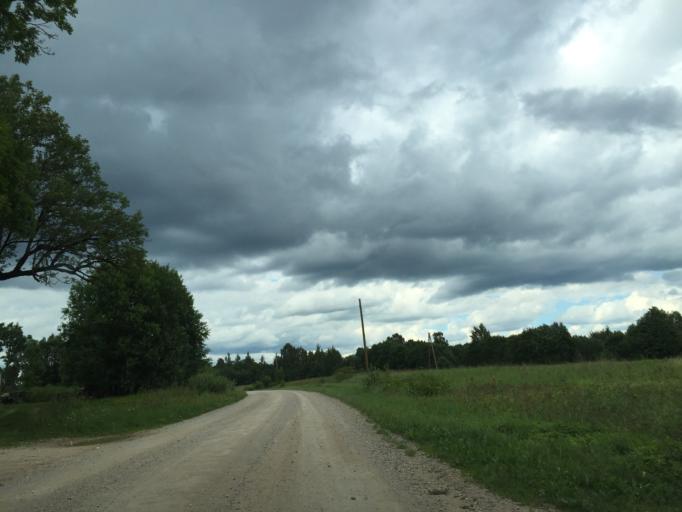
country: LV
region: Malpils
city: Malpils
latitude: 56.9312
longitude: 25.0135
